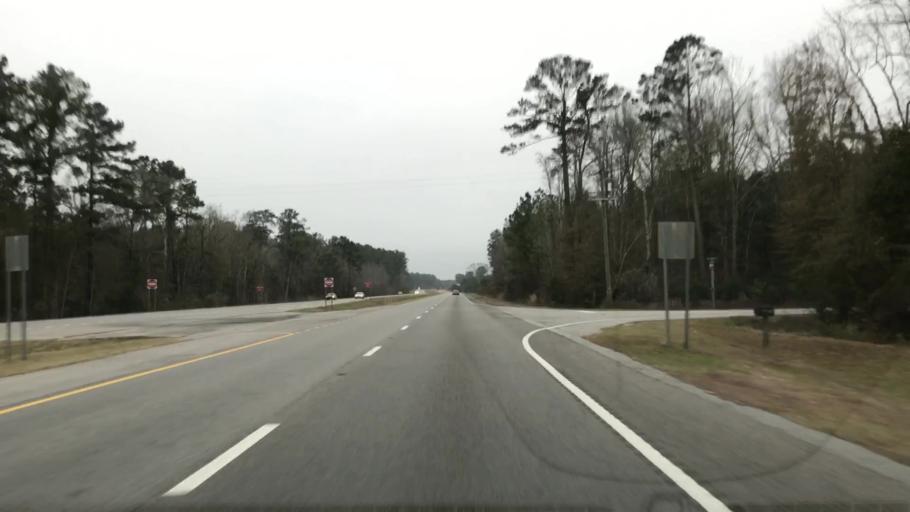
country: US
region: South Carolina
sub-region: Colleton County
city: Walterboro
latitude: 32.7257
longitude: -80.6005
